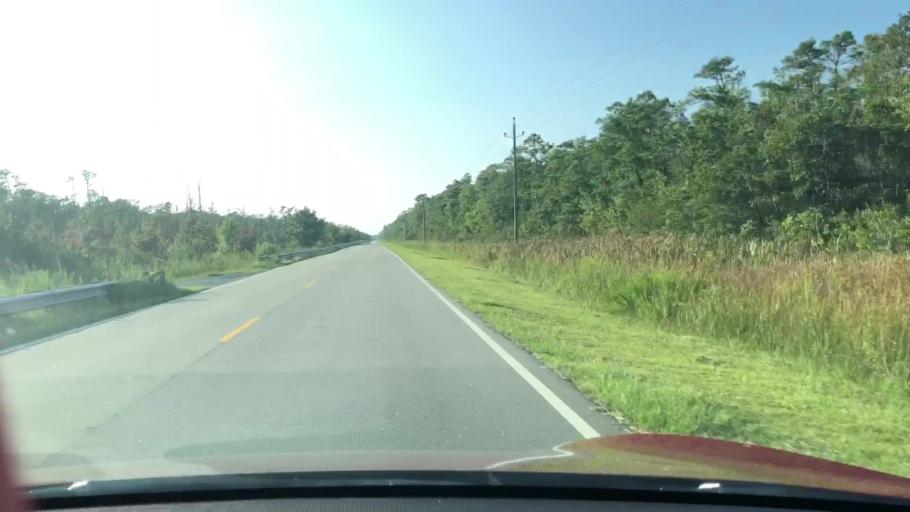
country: US
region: North Carolina
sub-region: Dare County
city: Manteo
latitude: 35.8110
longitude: -75.7912
